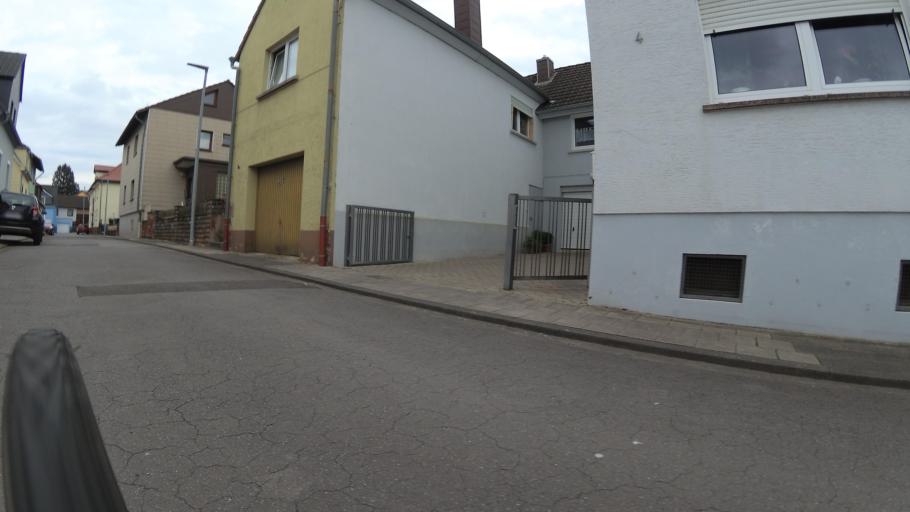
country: DE
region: Rheinland-Pfalz
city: Zweibrucken
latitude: 49.2445
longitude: 7.3502
